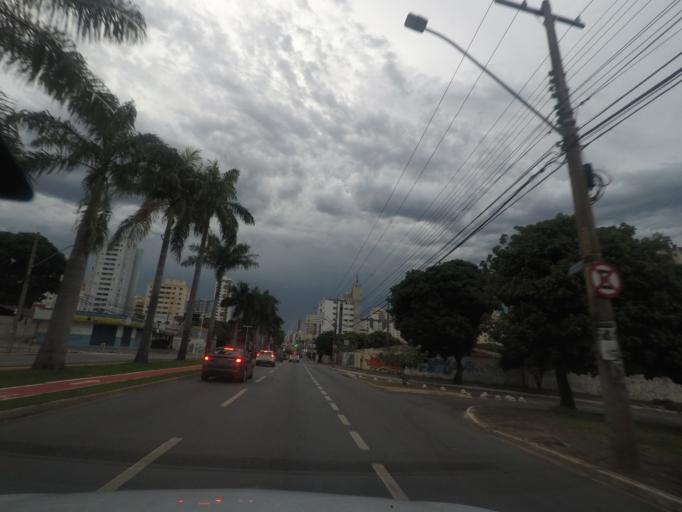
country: BR
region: Goias
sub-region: Goiania
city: Goiania
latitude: -16.7138
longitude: -49.2573
